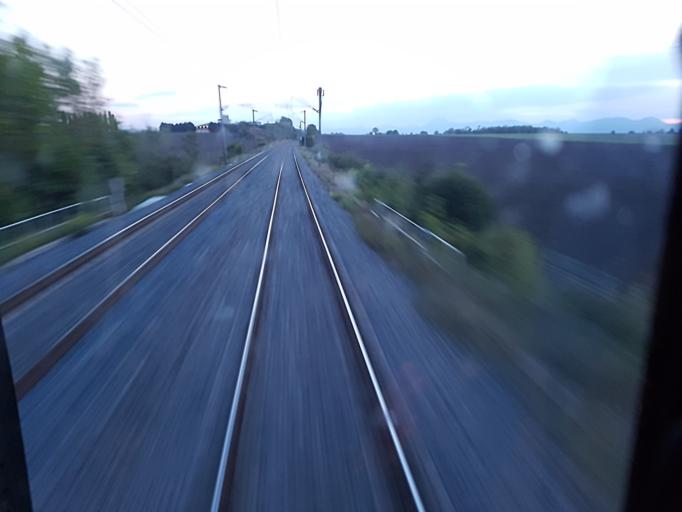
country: FR
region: Auvergne
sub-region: Departement du Puy-de-Dome
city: Ennezat
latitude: 45.9257
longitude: 3.2285
